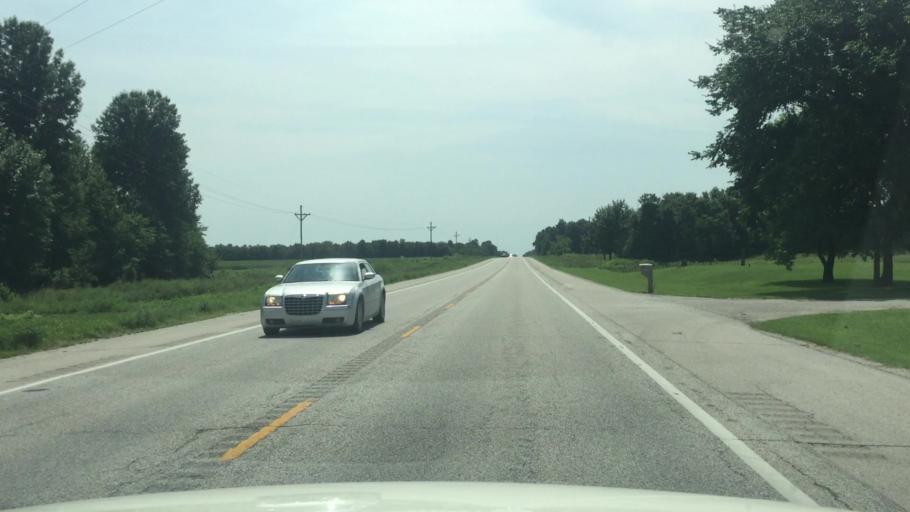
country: US
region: Kansas
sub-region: Cherokee County
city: Galena
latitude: 37.1588
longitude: -94.7043
